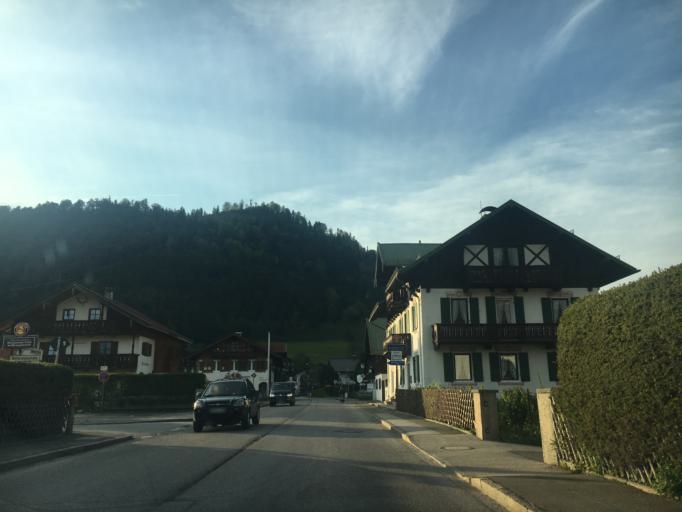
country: DE
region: Bavaria
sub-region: Upper Bavaria
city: Wallgau
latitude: 47.5192
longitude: 11.2829
